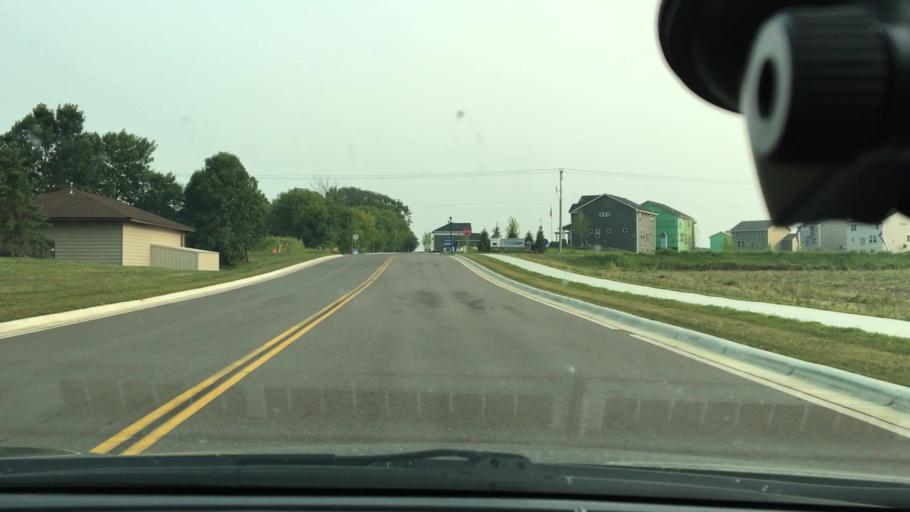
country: US
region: Minnesota
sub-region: Wright County
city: Saint Michael
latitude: 45.2111
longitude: -93.6292
